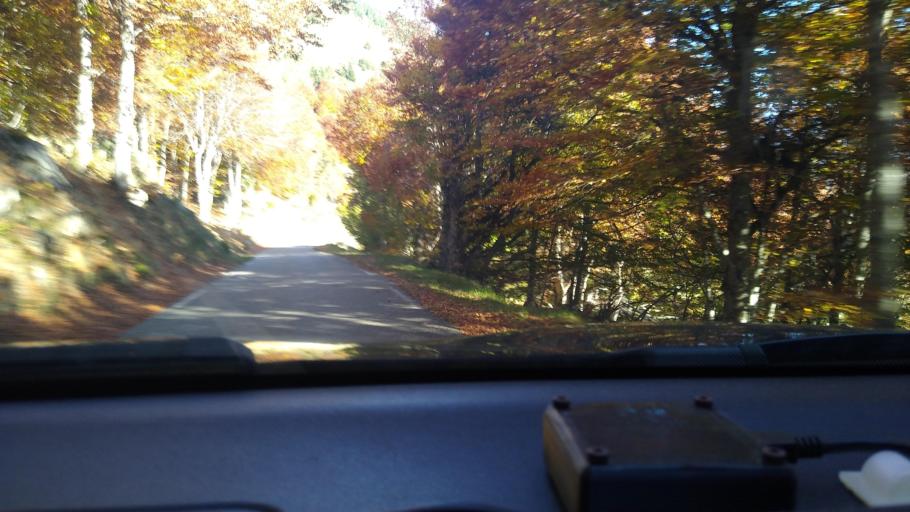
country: FR
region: Midi-Pyrenees
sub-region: Departement de l'Ariege
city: Ax-les-Thermes
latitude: 42.7297
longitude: 2.0184
